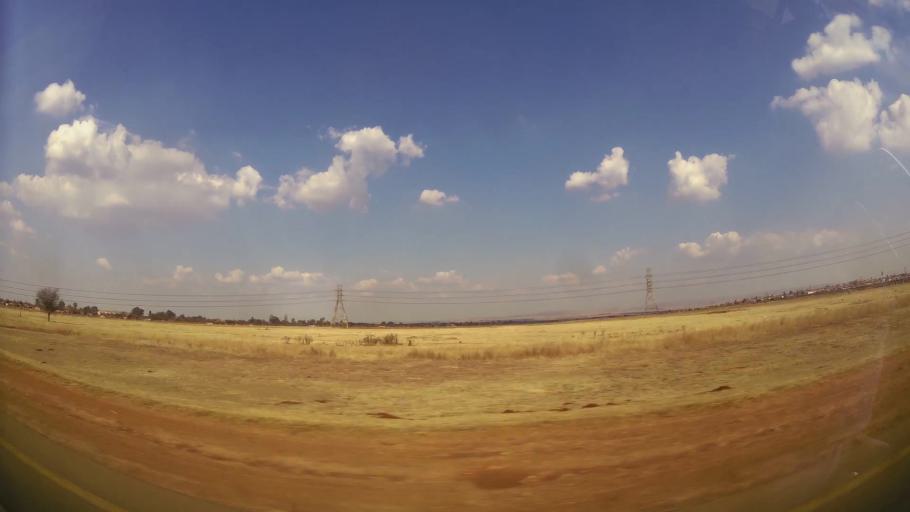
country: ZA
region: Gauteng
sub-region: Ekurhuleni Metropolitan Municipality
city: Germiston
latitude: -26.3386
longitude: 28.2263
